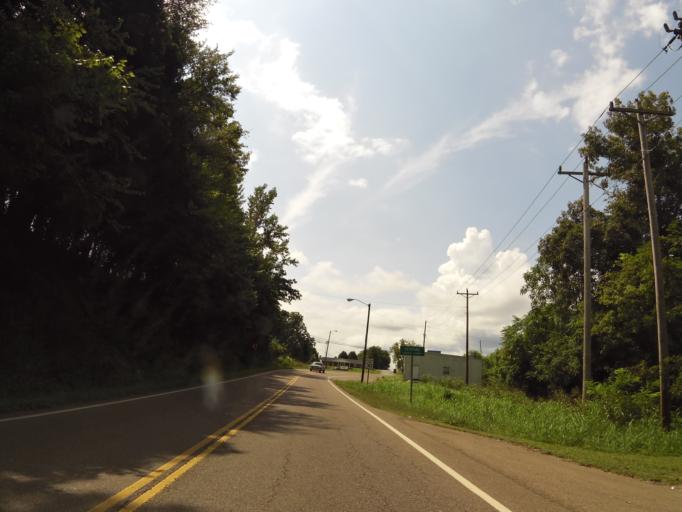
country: US
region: Tennessee
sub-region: Perry County
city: Linden
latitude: 35.6184
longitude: -87.8356
